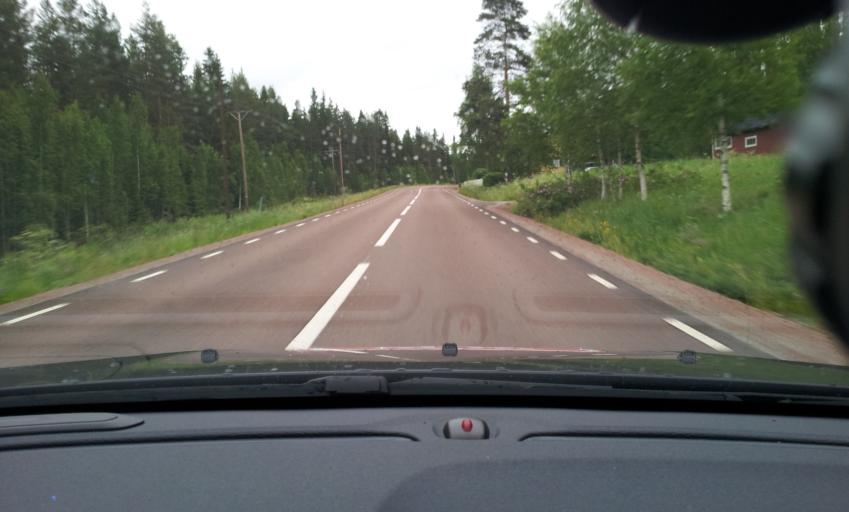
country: SE
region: Jaemtland
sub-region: Ragunda Kommun
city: Hammarstrand
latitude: 63.0600
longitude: 16.4362
